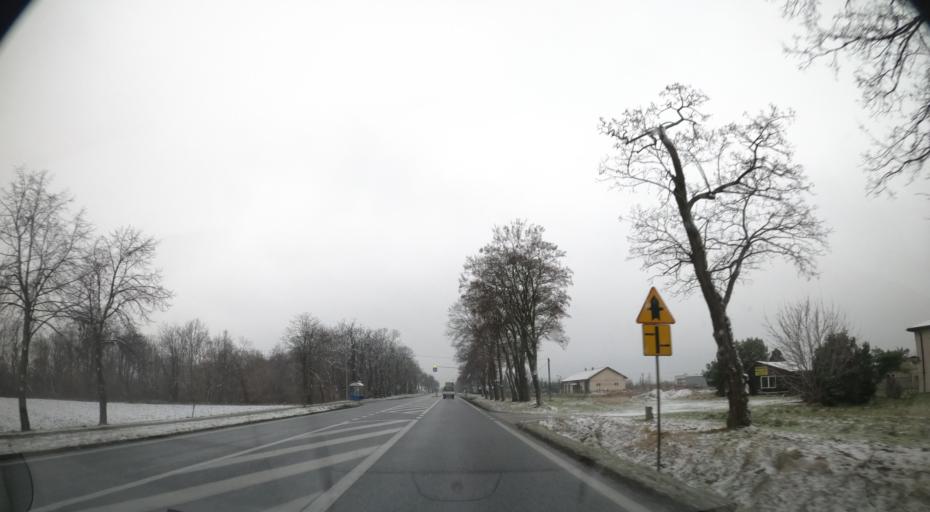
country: PL
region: Masovian Voivodeship
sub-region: Powiat warszawski zachodni
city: Bieniewice
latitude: 52.2057
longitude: 20.4982
